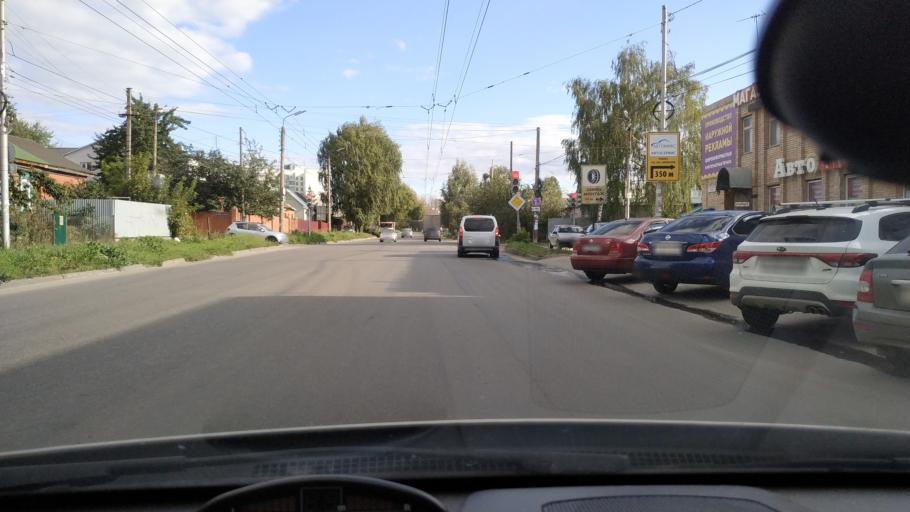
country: RU
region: Rjazan
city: Ryazan'
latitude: 54.6118
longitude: 39.6970
